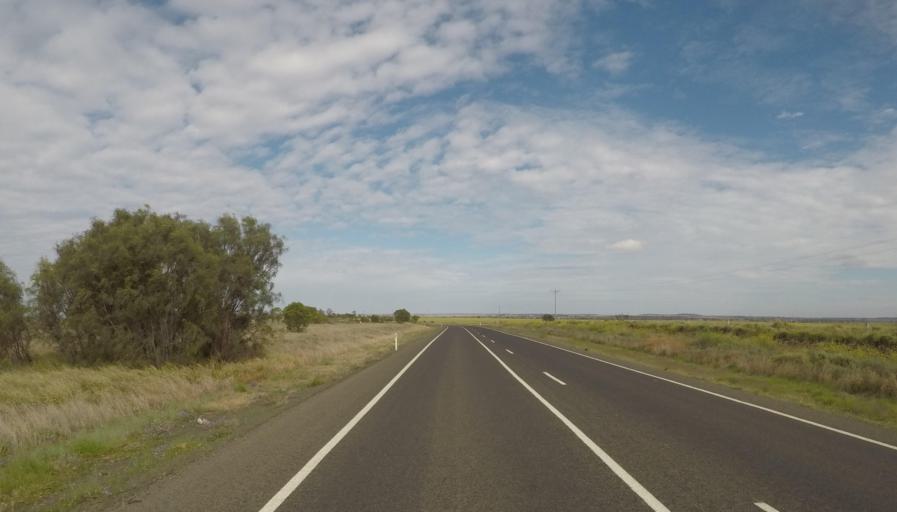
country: AU
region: Queensland
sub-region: Western Downs
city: Westcourt
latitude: -26.6429
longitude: 149.8080
